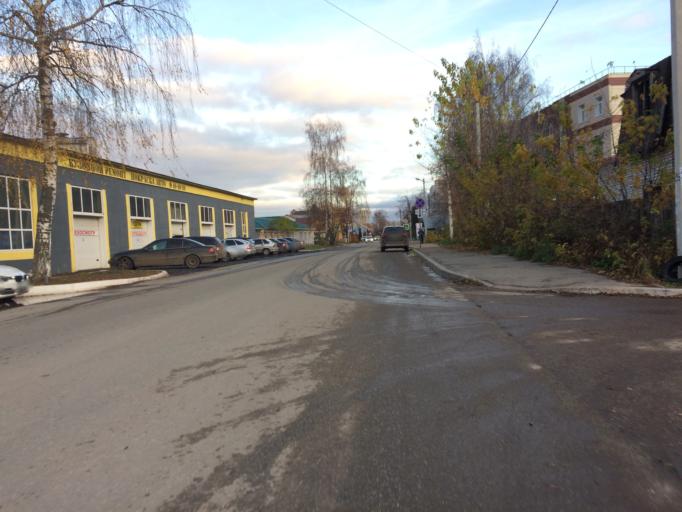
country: RU
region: Mariy-El
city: Yoshkar-Ola
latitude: 56.6464
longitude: 47.9007
